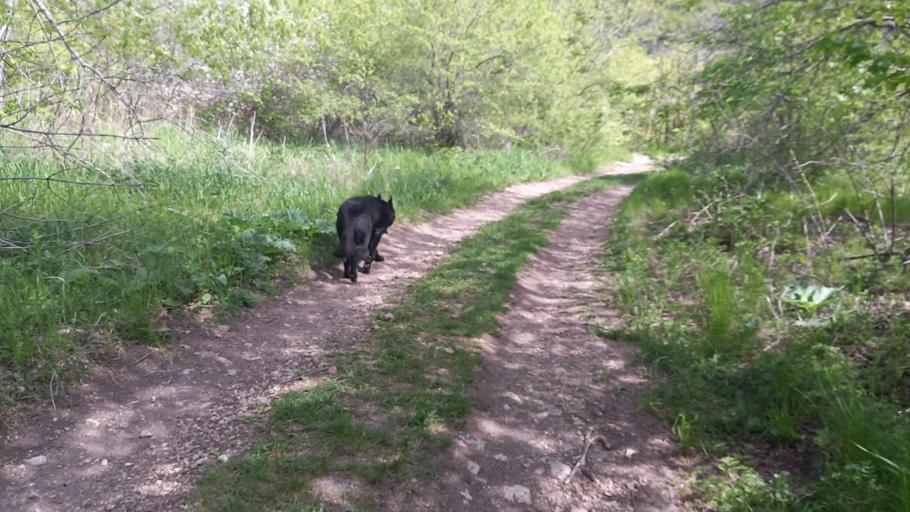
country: RU
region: Stavropol'skiy
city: Pyatigorsk
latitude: 44.0897
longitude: 43.0297
